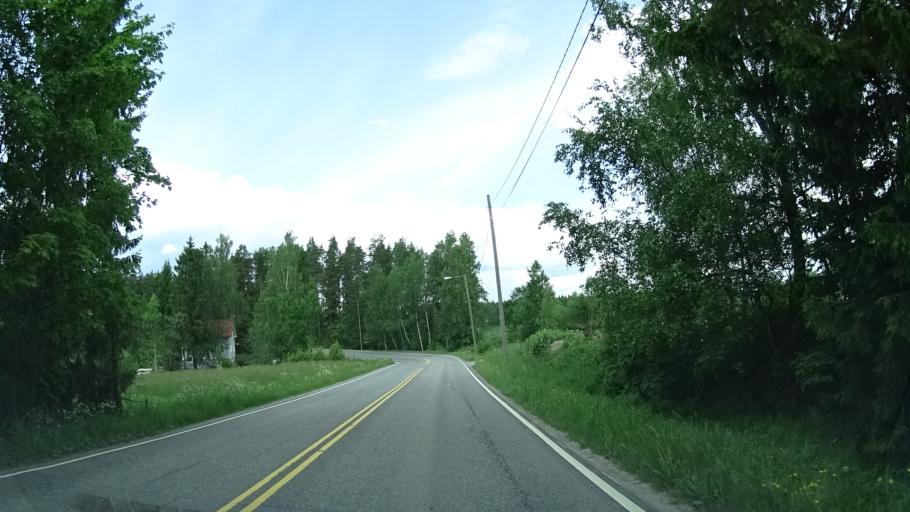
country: FI
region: Uusimaa
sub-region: Helsinki
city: Kirkkonummi
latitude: 60.2152
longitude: 24.4825
